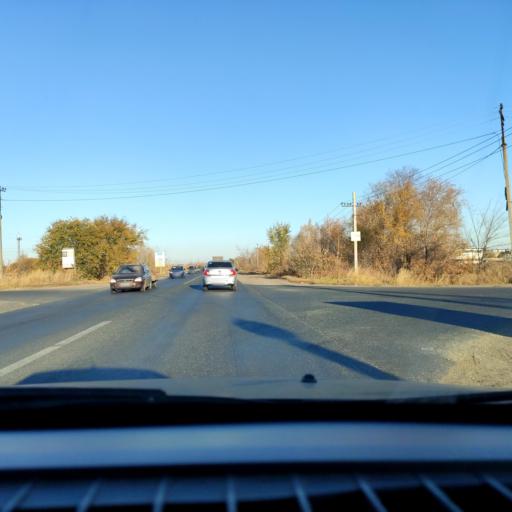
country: RU
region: Samara
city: Tol'yatti
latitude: 53.5654
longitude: 49.3510
